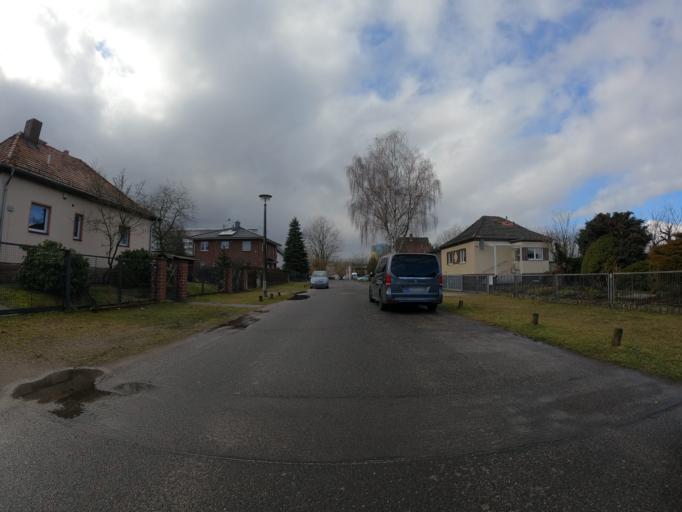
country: DE
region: Berlin
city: Marzahn
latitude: 52.5319
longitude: 13.5568
